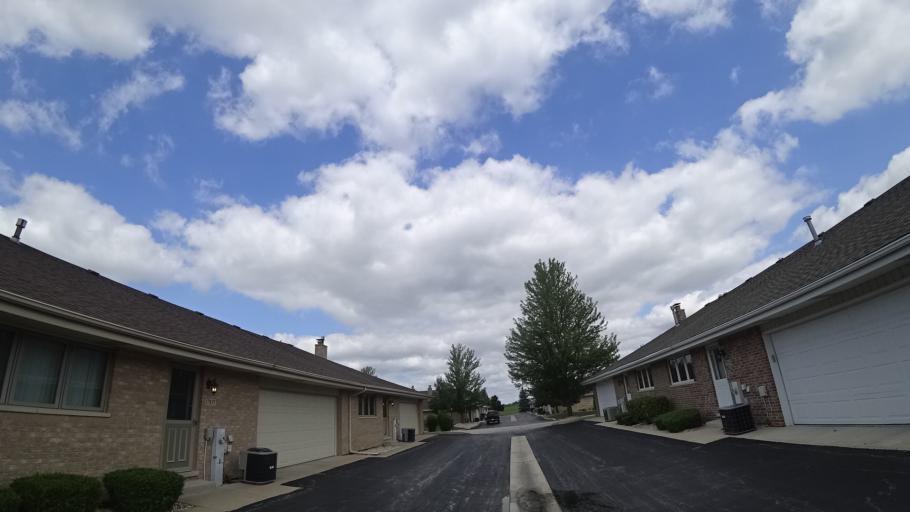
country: US
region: Illinois
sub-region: Will County
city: Mokena
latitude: 41.5652
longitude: -87.8788
